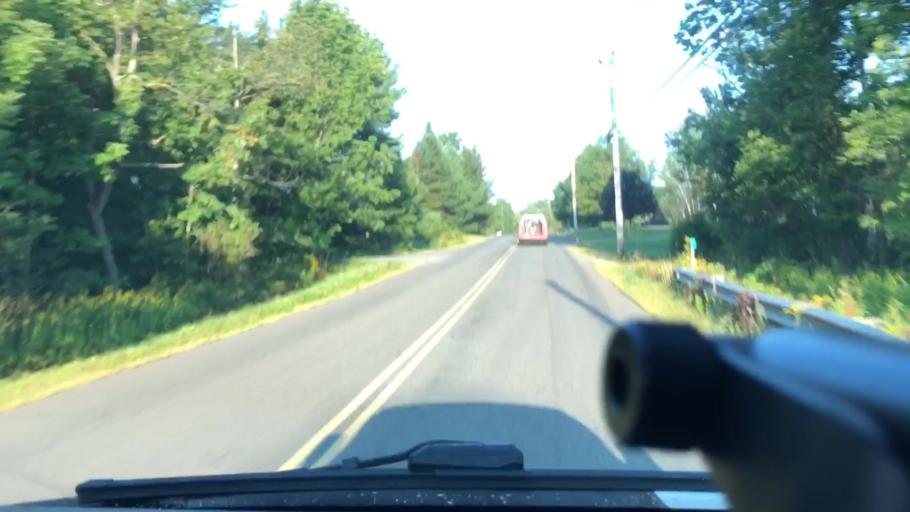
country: US
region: Massachusetts
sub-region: Franklin County
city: Ashfield
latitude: 42.5107
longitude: -72.8159
